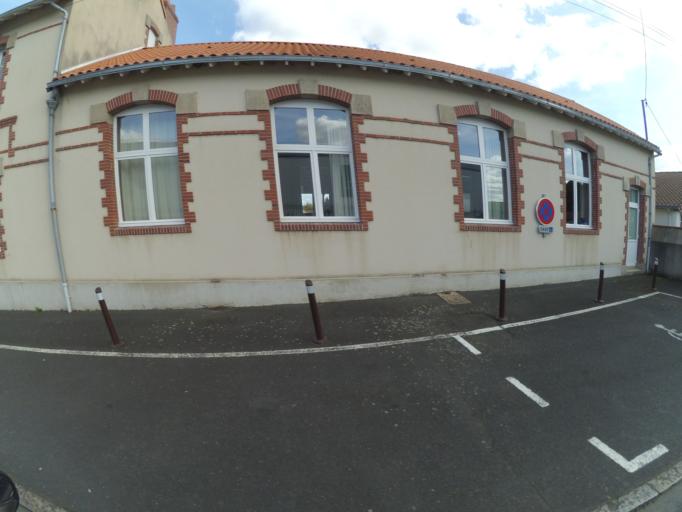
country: FR
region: Pays de la Loire
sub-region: Departement de la Loire-Atlantique
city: La Chapelle-Heulin
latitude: 47.1742
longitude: -1.3423
